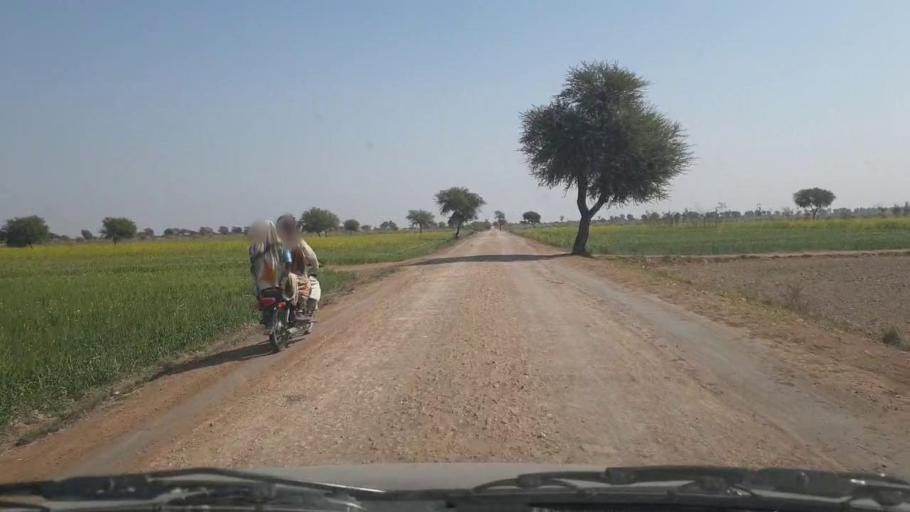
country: PK
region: Sindh
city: Samaro
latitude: 25.2433
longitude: 69.3678
